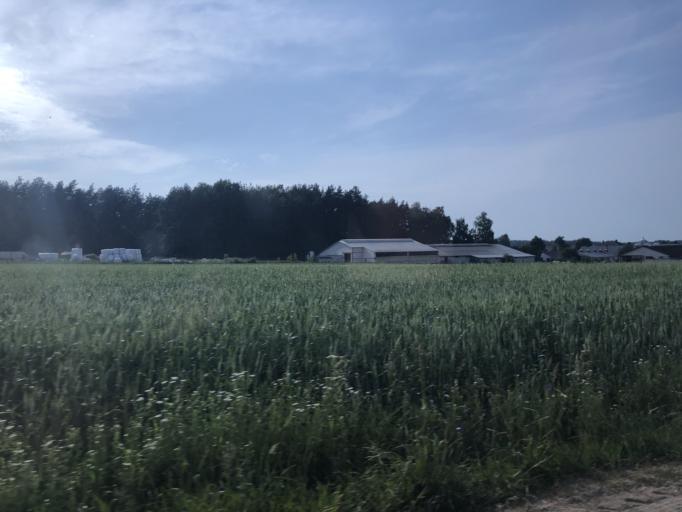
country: PL
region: Podlasie
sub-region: Lomza
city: Lomza
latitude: 53.1419
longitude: 22.0064
